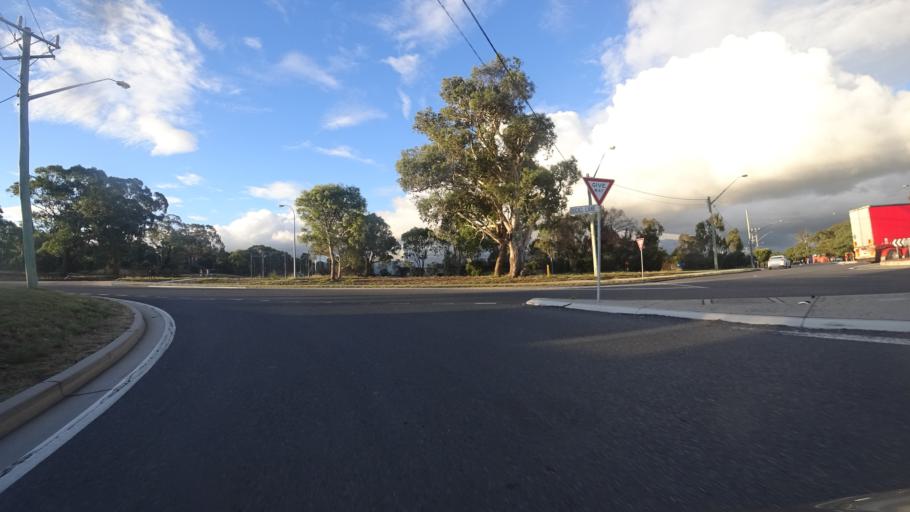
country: AU
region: New South Wales
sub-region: Goulburn Mulwaree
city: Goulburn
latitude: -34.7724
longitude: 149.6909
